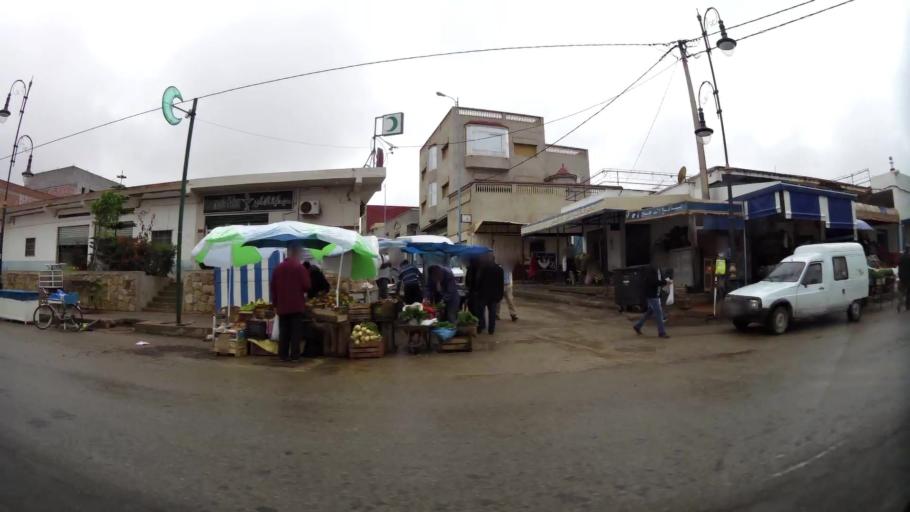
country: MA
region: Taza-Al Hoceima-Taounate
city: Imzourene
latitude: 35.1735
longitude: -3.8652
